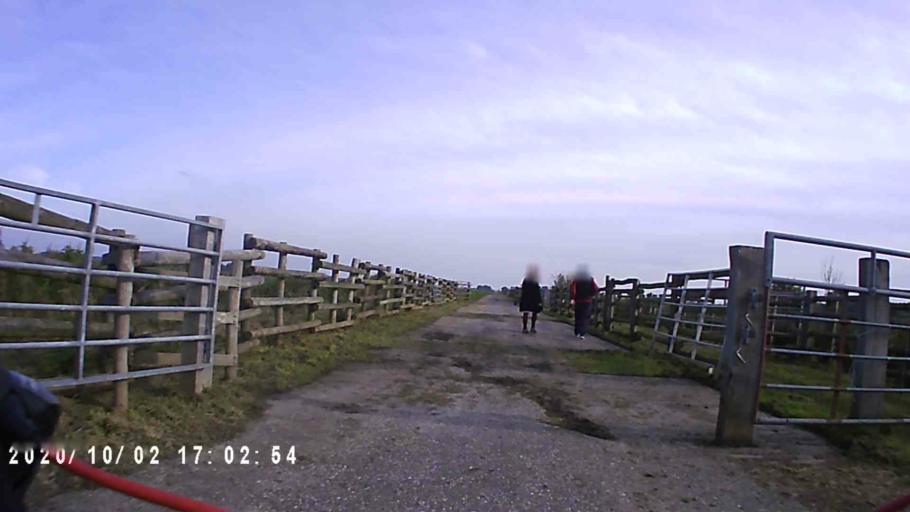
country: NL
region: Groningen
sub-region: Gemeente De Marne
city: Ulrum
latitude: 53.3424
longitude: 6.2626
